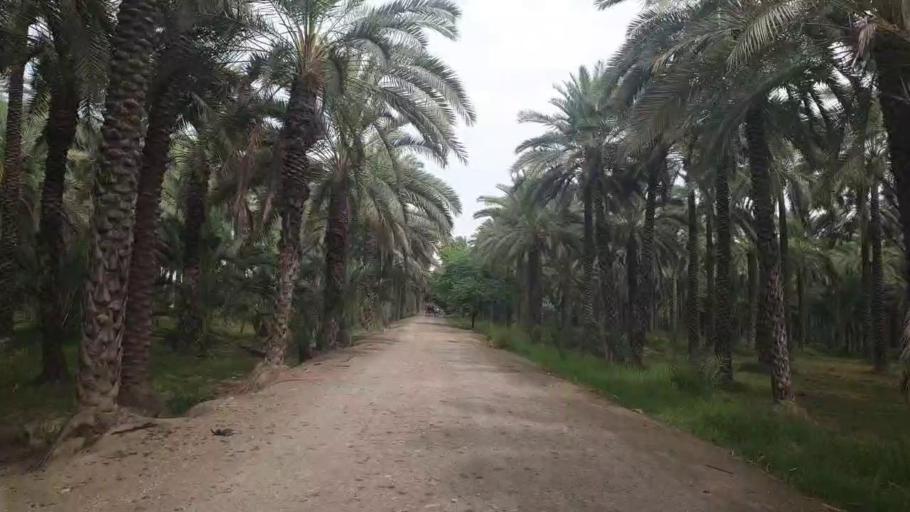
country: PK
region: Sindh
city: Sukkur
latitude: 27.6414
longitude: 68.8233
